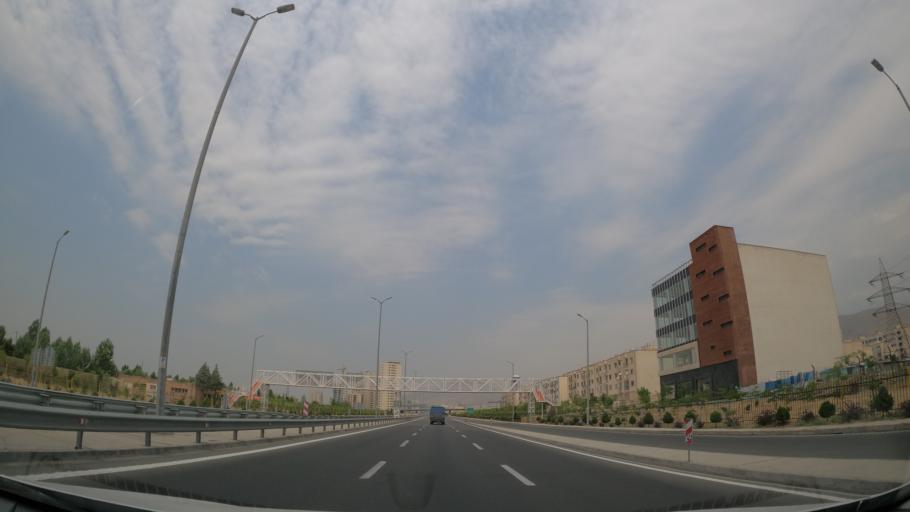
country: IR
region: Tehran
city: Shahr-e Qods
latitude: 35.7398
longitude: 51.2500
